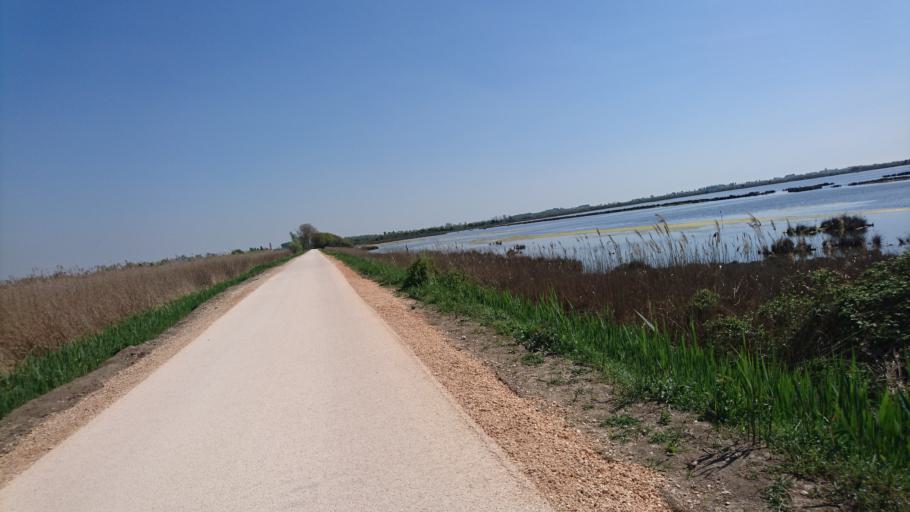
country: IT
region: Veneto
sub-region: Provincia di Venezia
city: Musile di Piave
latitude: 45.5744
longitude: 12.5313
